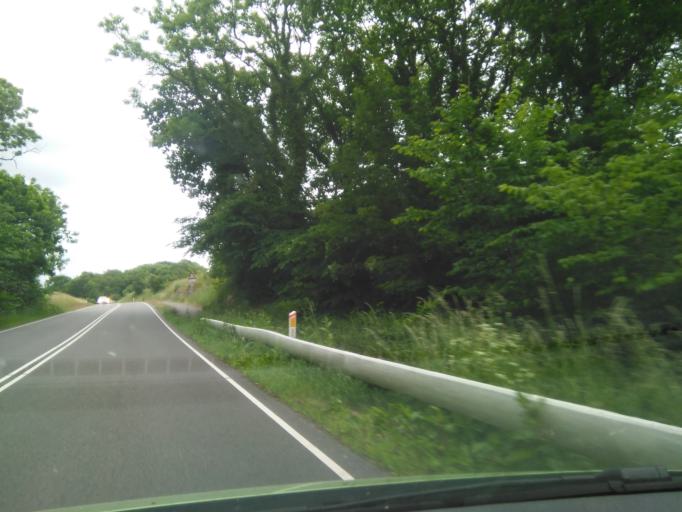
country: DK
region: Capital Region
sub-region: Bornholm Kommune
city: Akirkeby
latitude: 55.2241
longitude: 14.8906
